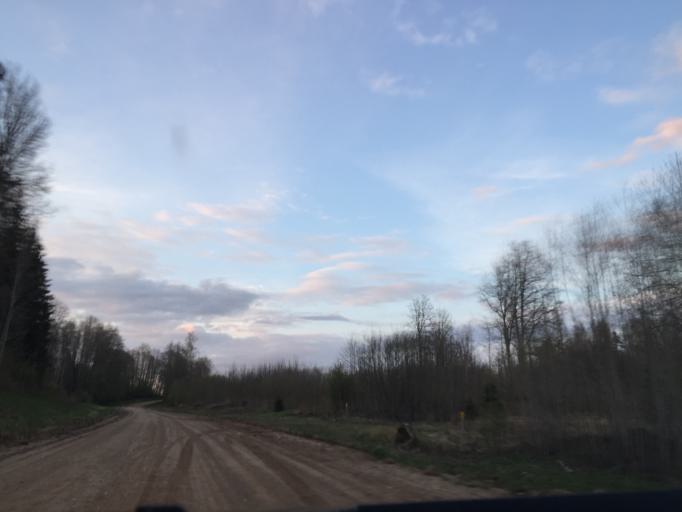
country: LV
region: Aluksnes Rajons
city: Aluksne
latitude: 57.3110
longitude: 26.9152
